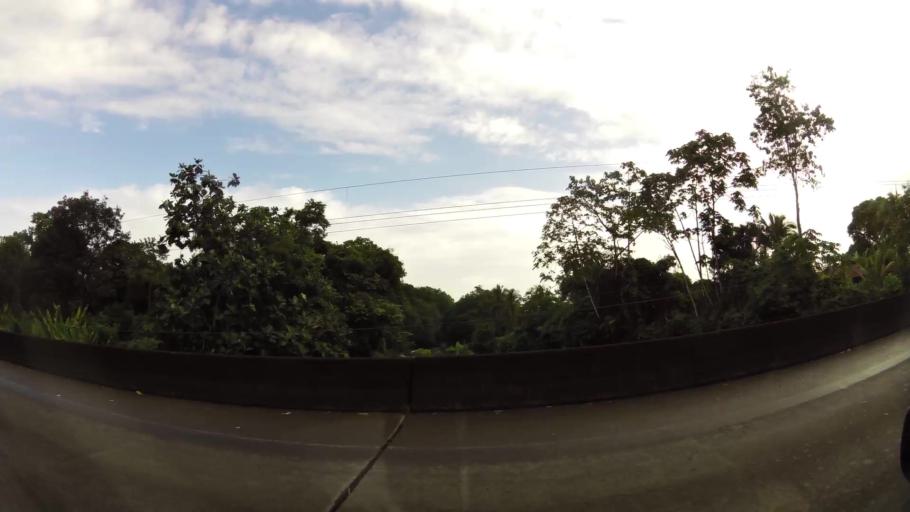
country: CR
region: Limon
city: Pocora
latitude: 10.1709
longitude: -83.6083
